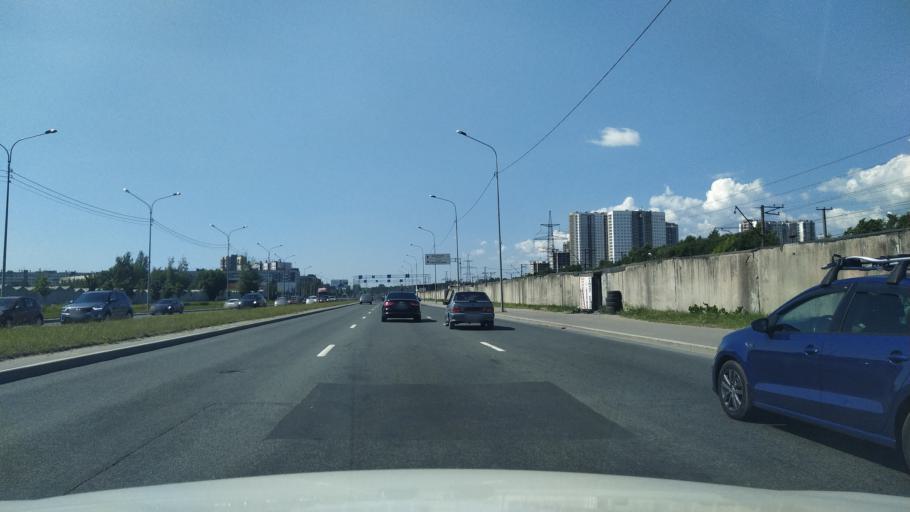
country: RU
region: Leningrad
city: Parnas
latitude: 60.0642
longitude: 30.3247
